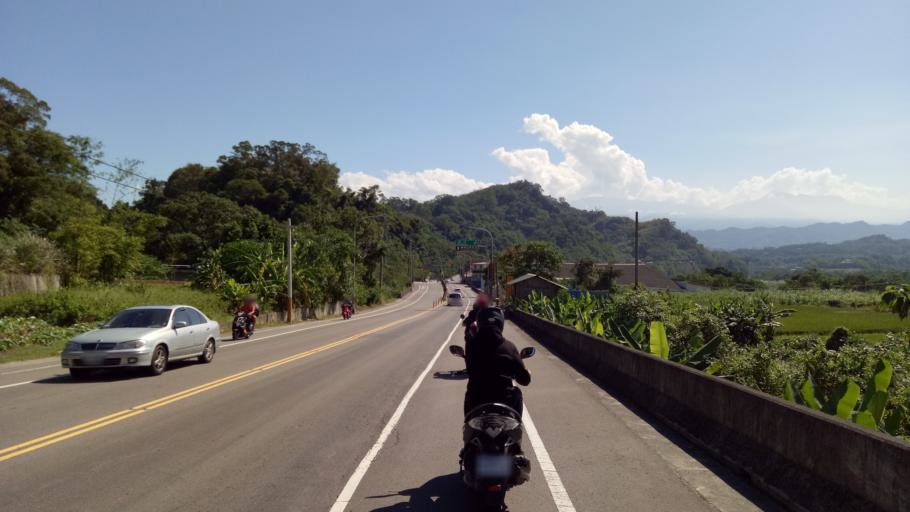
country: TW
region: Taiwan
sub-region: Hsinchu
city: Hsinchu
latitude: 24.6837
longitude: 120.9626
